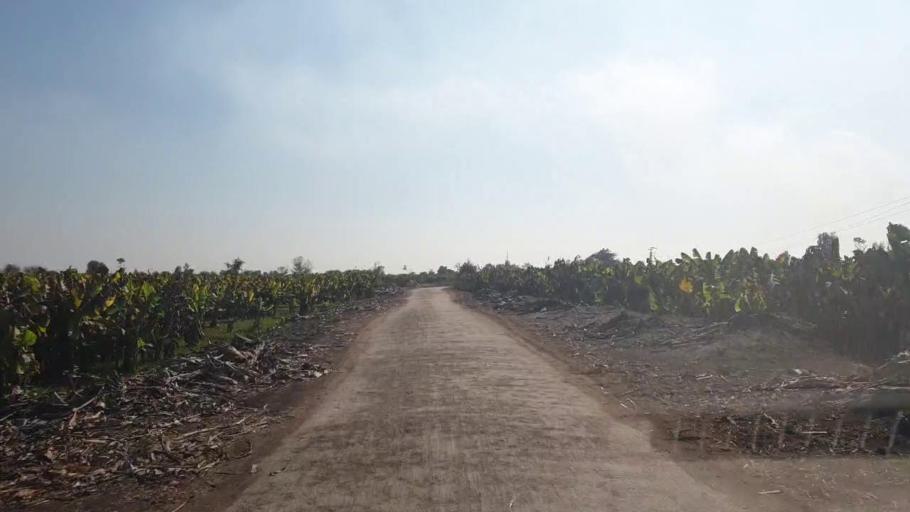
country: PK
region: Sindh
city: Shahdadpur
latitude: 25.9170
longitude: 68.5777
